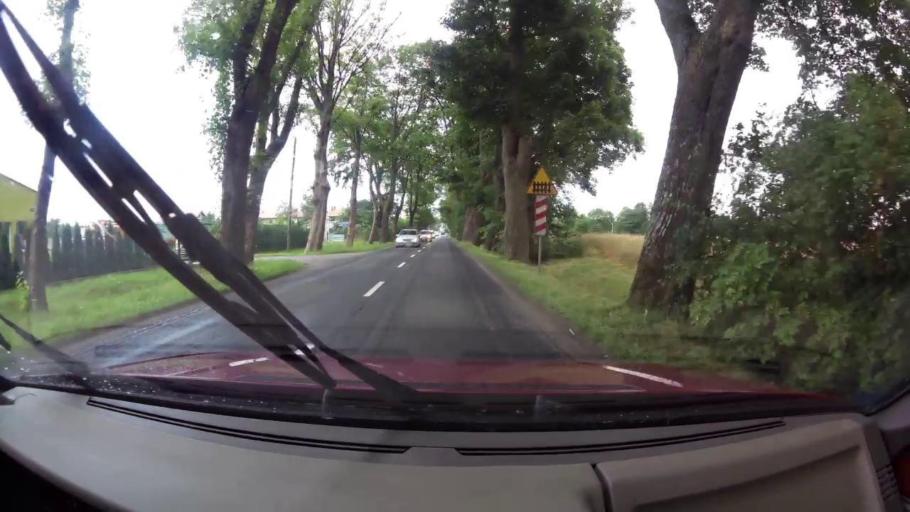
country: PL
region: West Pomeranian Voivodeship
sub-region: Koszalin
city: Koszalin
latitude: 54.1756
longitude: 16.1631
